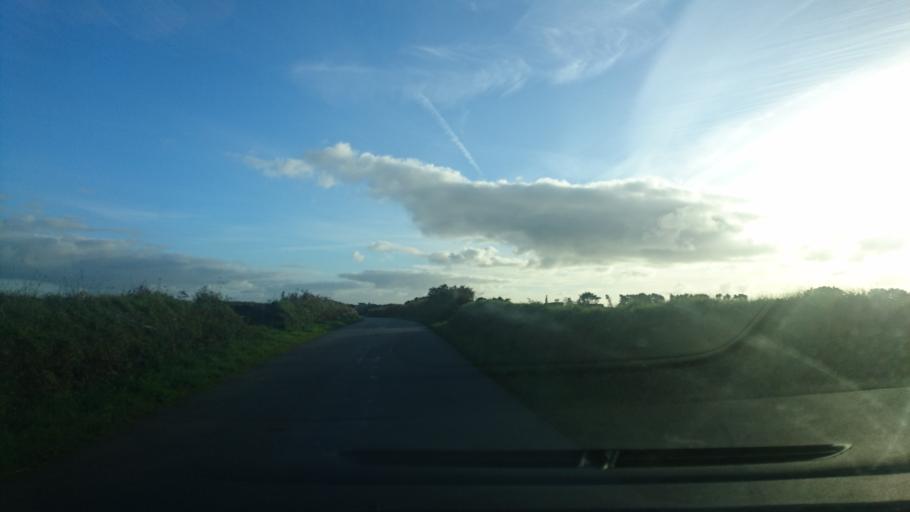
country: FR
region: Brittany
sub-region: Departement du Finistere
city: Lampaul-Plouarzel
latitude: 48.4297
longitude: -4.7694
